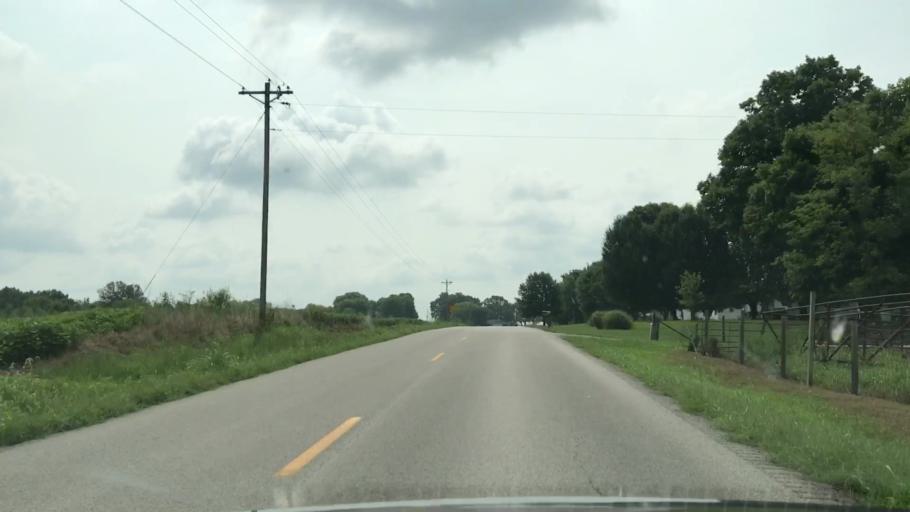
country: US
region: Kentucky
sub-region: Edmonson County
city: Brownsville
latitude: 37.1359
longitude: -86.1755
